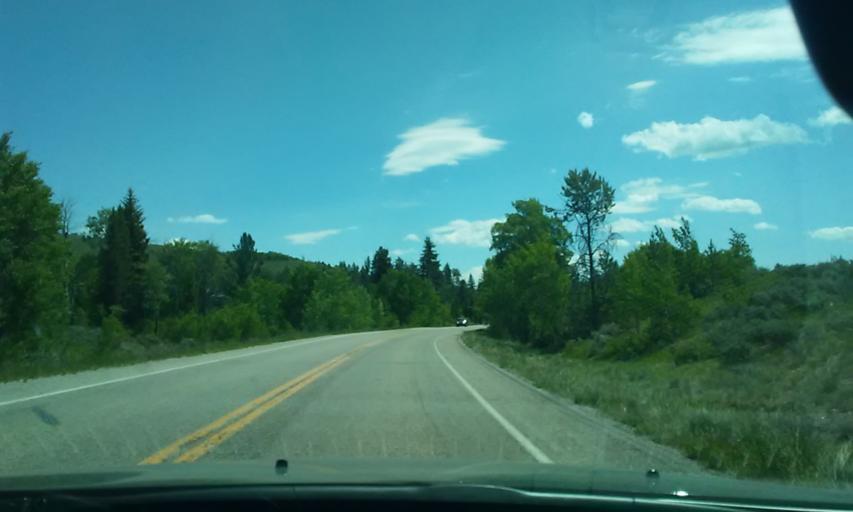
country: US
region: Wyoming
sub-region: Teton County
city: Jackson
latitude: 43.8389
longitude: -110.4771
